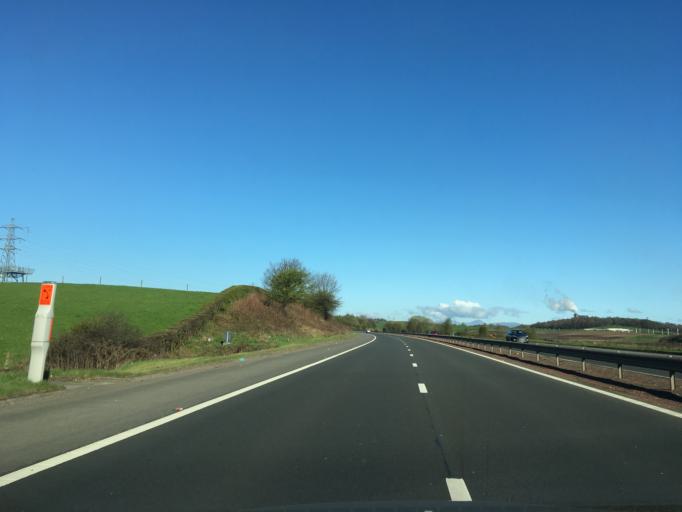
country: GB
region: Scotland
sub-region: Stirling
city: Cowie
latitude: 56.0606
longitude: -3.8573
